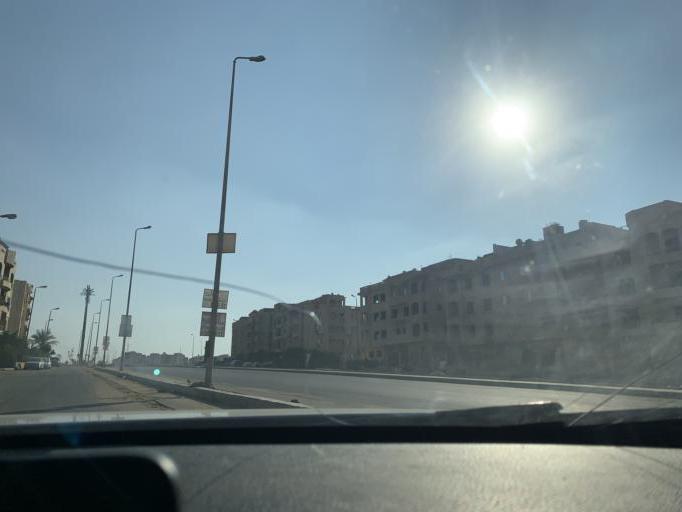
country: EG
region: Muhafazat al Qalyubiyah
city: Al Khankah
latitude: 30.0019
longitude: 31.4807
